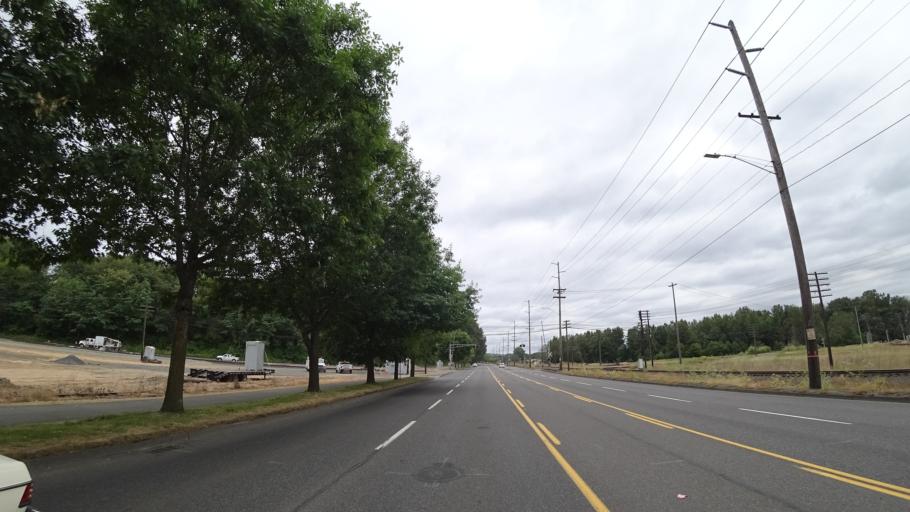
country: US
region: Washington
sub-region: Clark County
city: Vancouver
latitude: 45.5925
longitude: -122.7111
